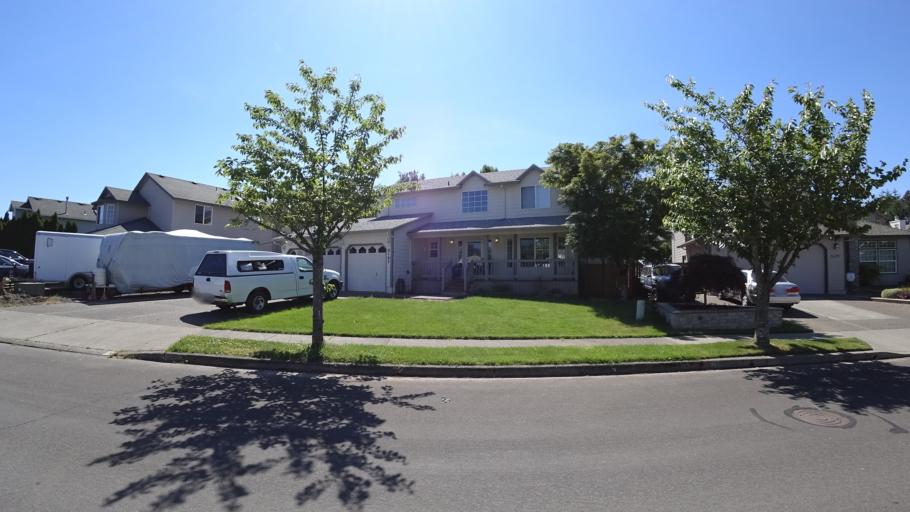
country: US
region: Oregon
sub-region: Multnomah County
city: Gresham
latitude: 45.4739
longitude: -122.4640
